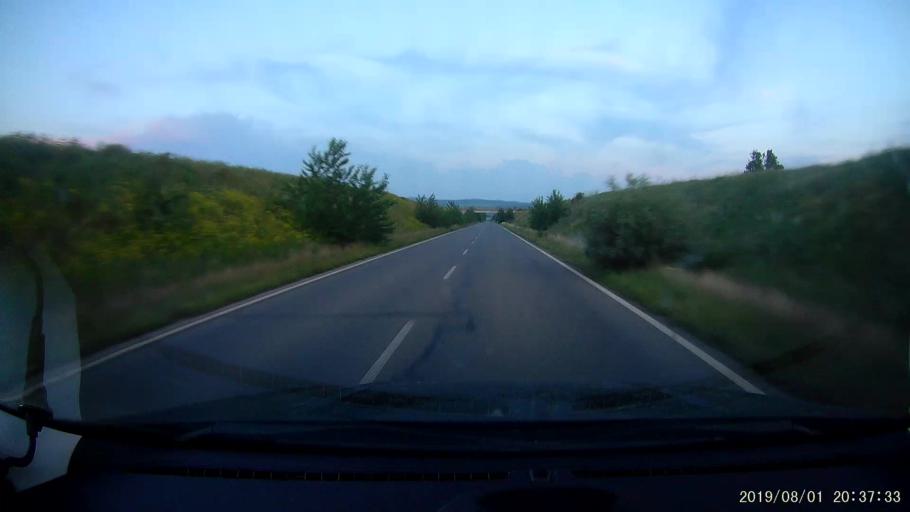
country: BG
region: Yambol
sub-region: Obshtina Elkhovo
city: Elkhovo
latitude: 42.0456
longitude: 26.5947
